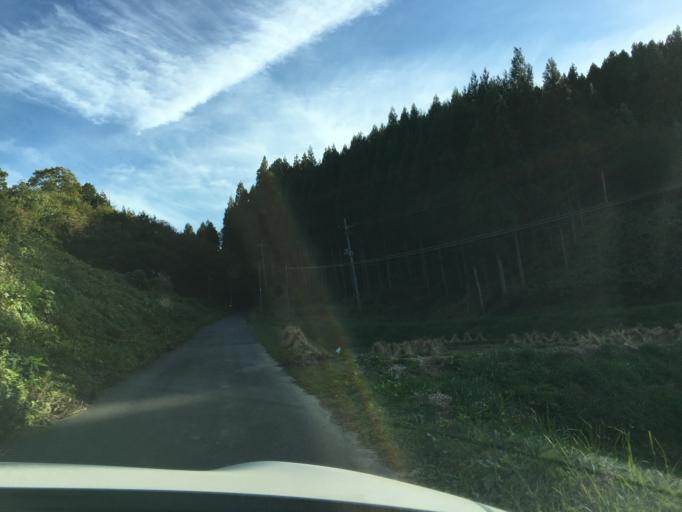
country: JP
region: Fukushima
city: Ishikawa
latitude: 37.2434
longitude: 140.6082
